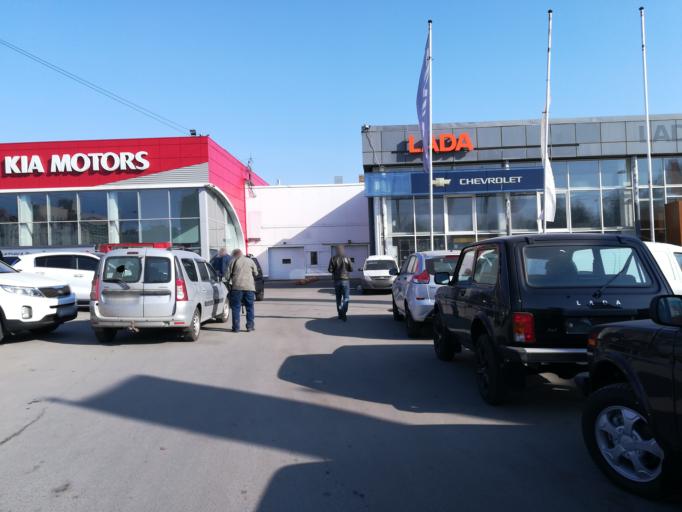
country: RU
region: St.-Petersburg
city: Vasyl'evsky Ostrov
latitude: 59.9553
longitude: 30.2383
